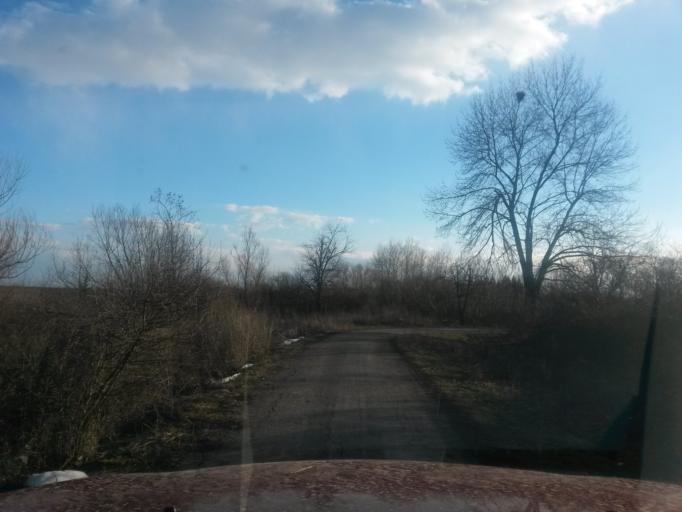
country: SK
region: Kosicky
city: Sobrance
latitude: 48.7761
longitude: 22.0867
